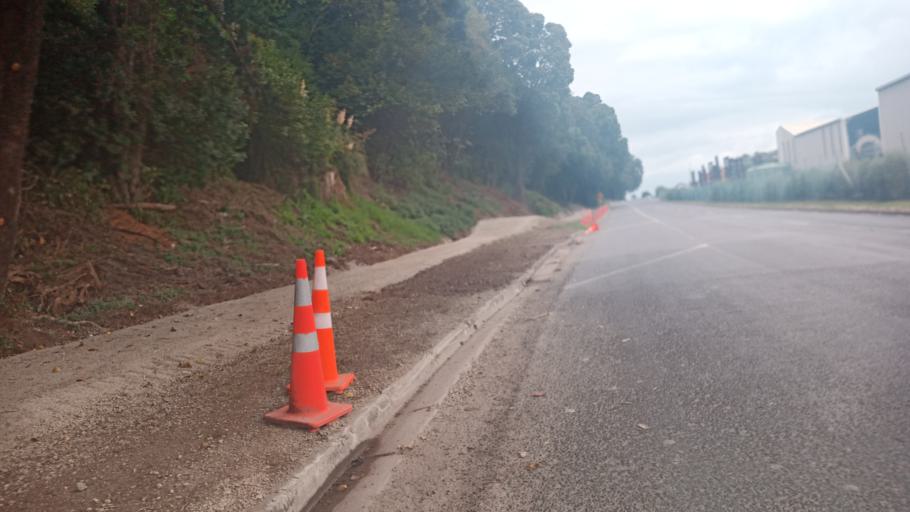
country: NZ
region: Gisborne
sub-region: Gisborne District
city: Gisborne
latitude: -38.6766
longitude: 178.0263
